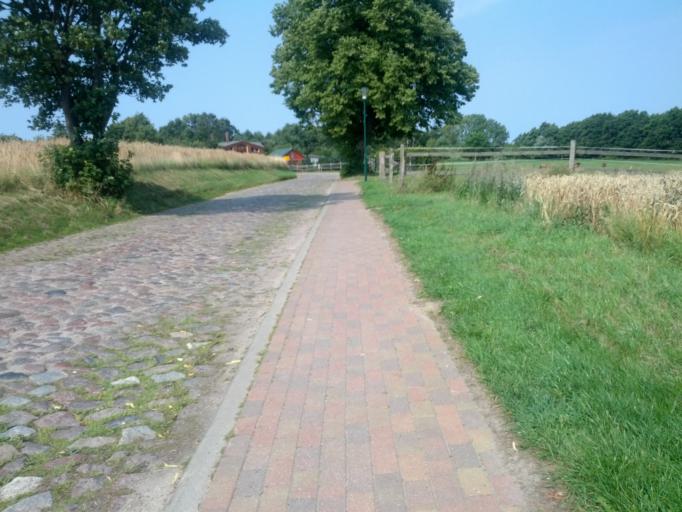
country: DE
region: Mecklenburg-Vorpommern
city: Bastorf
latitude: 54.1161
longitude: 11.6812
